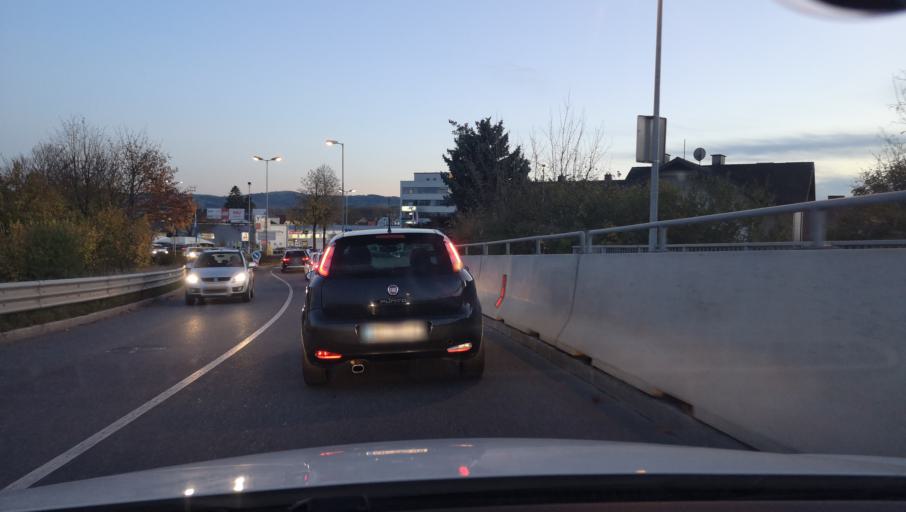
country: AT
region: Lower Austria
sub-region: Politischer Bezirk Amstetten
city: Amstetten
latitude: 48.1206
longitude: 14.8948
